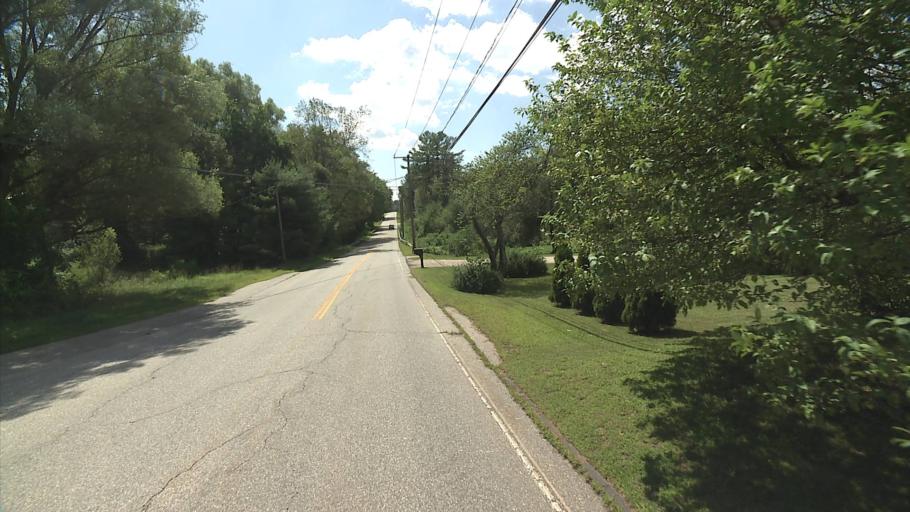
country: US
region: Connecticut
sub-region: Windham County
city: Windham
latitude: 41.7445
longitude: -72.1565
